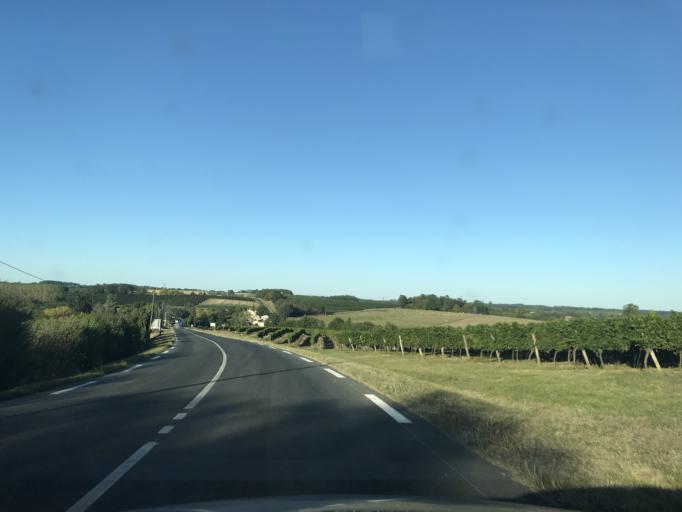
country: FR
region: Aquitaine
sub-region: Departement de la Gironde
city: Sauveterre-de-Guyenne
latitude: 44.6960
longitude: -0.0811
